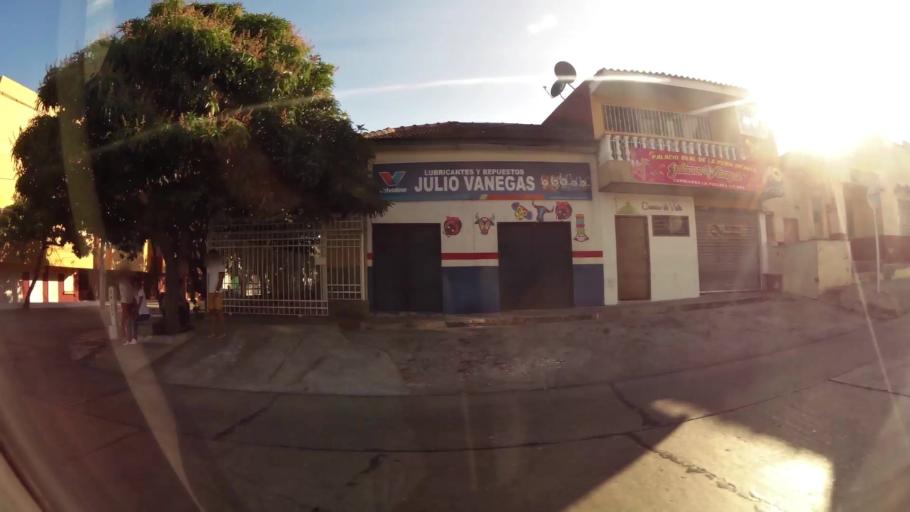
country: CO
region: Atlantico
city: Barranquilla
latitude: 10.9867
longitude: -74.7936
